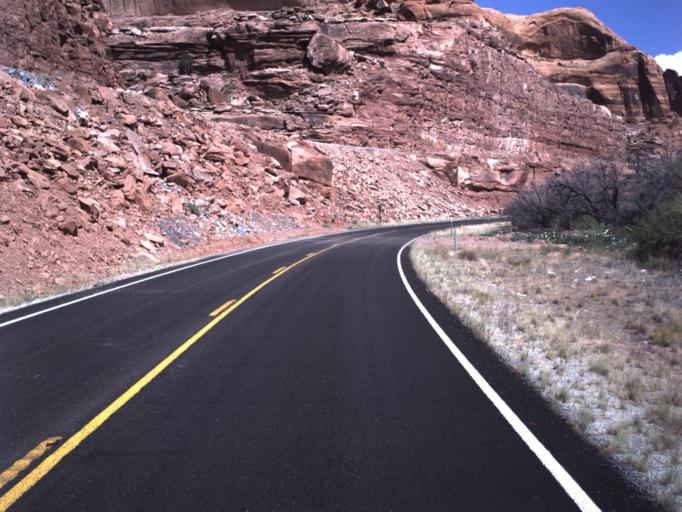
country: US
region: Utah
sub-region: Grand County
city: Moab
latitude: 38.5793
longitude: -109.6438
